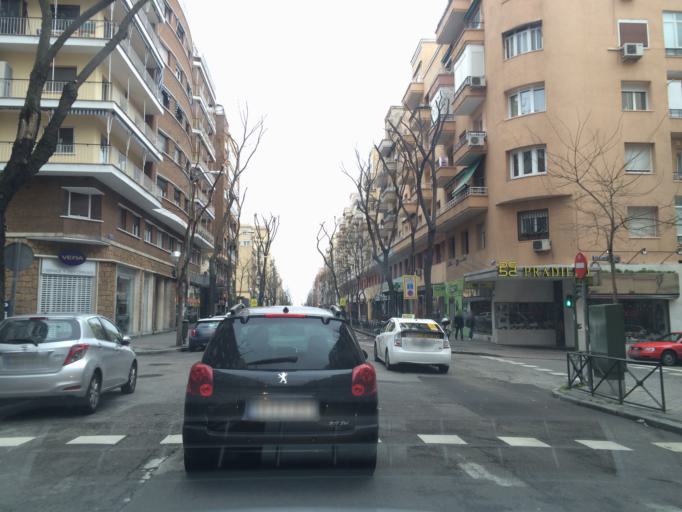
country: ES
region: Madrid
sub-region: Provincia de Madrid
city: Chamberi
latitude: 40.4379
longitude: -3.7130
